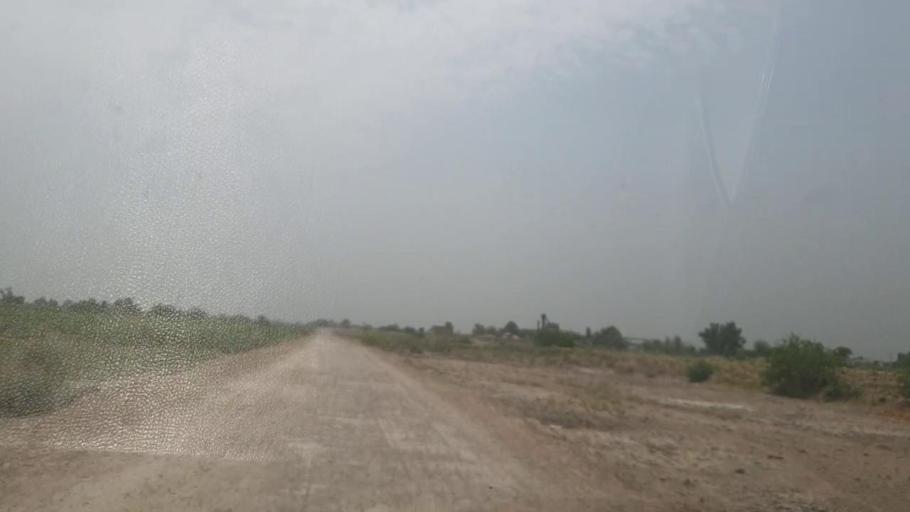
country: PK
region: Sindh
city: Kot Diji
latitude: 27.4317
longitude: 68.6268
